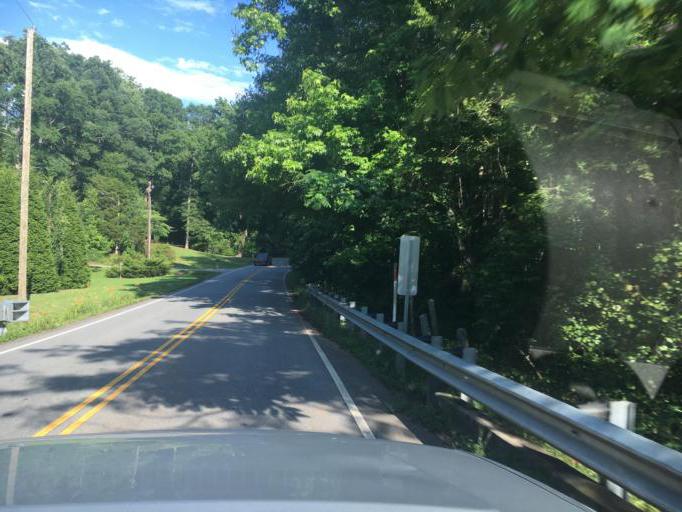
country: US
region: South Carolina
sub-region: Greenville County
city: Simpsonville
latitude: 34.7735
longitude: -82.2680
